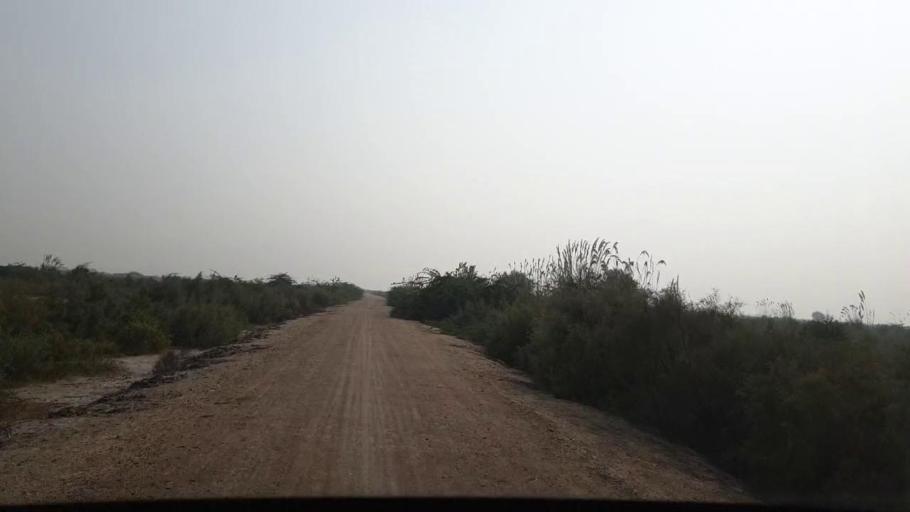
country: PK
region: Sindh
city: Jati
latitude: 24.2776
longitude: 68.4231
